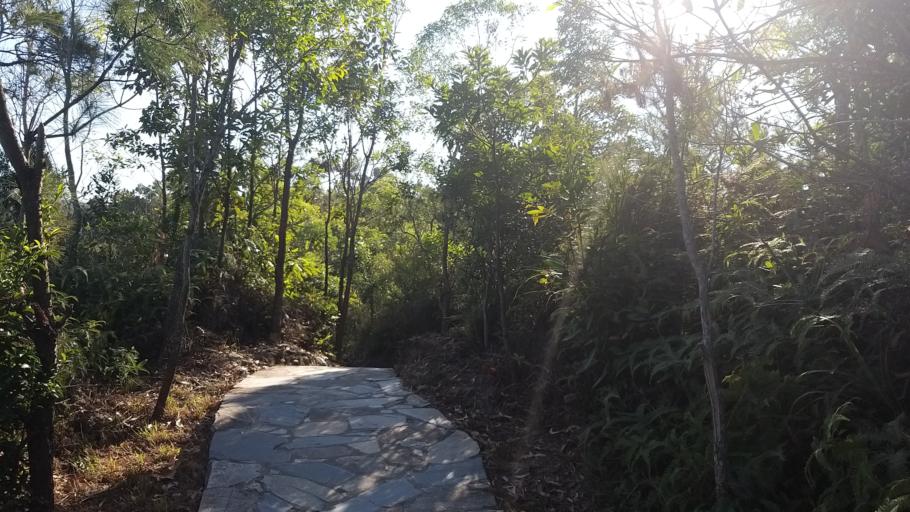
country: HK
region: Tuen Mun
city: Tuen Mun
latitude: 22.4022
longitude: 113.9883
